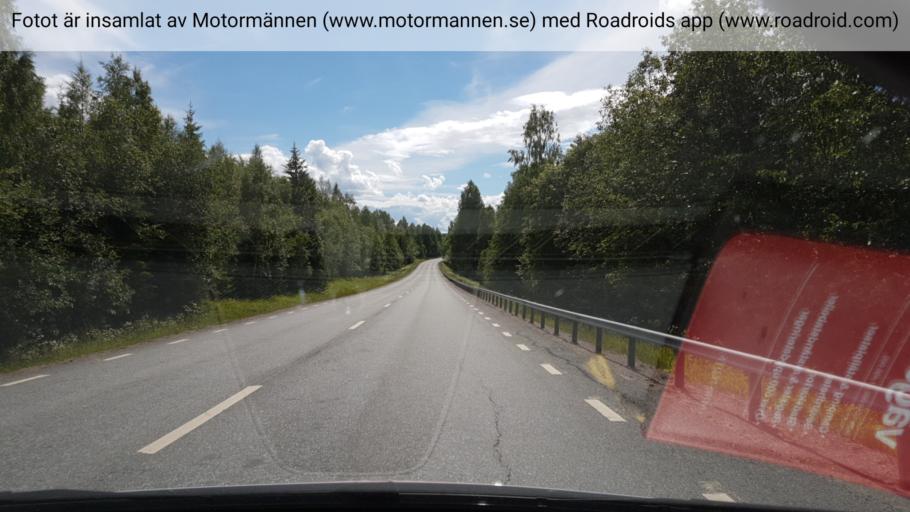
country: SE
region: Vaesternorrland
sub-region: Solleftea Kommun
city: Solleftea
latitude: 63.2842
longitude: 17.2216
